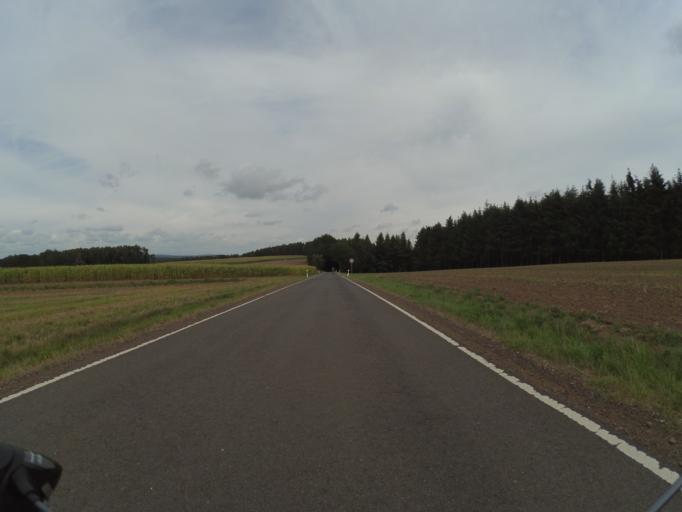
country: DE
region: Rheinland-Pfalz
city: Niersbach
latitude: 49.9311
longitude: 6.7563
